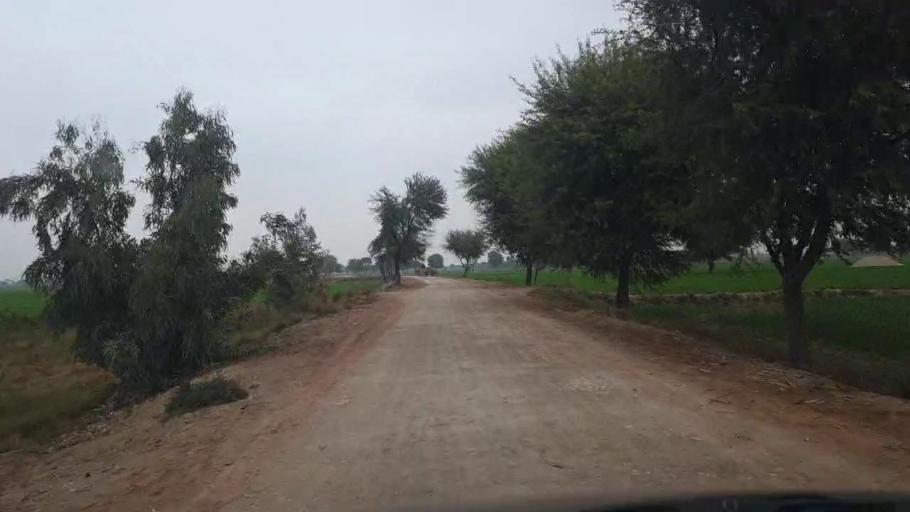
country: PK
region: Sindh
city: Shahdadpur
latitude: 25.9661
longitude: 68.7126
